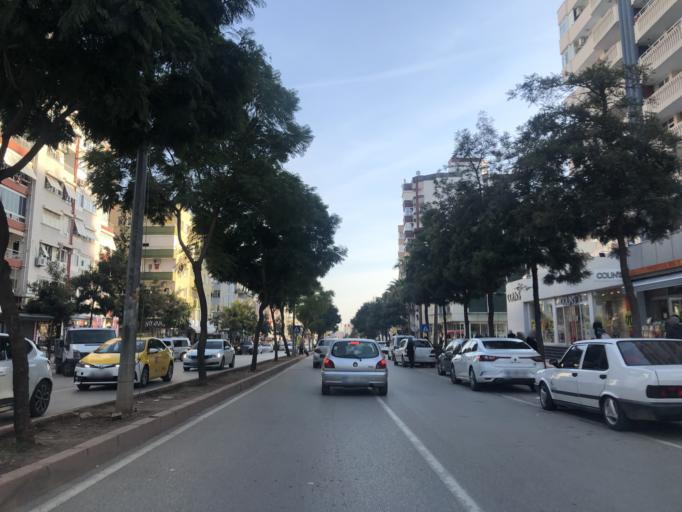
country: TR
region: Adana
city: Adana
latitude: 37.0396
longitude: 35.3046
